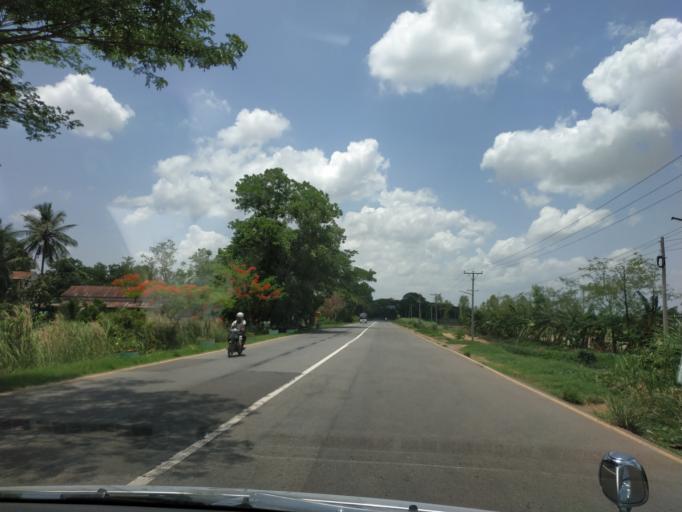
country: MM
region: Bago
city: Thanatpin
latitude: 17.4908
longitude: 96.6842
